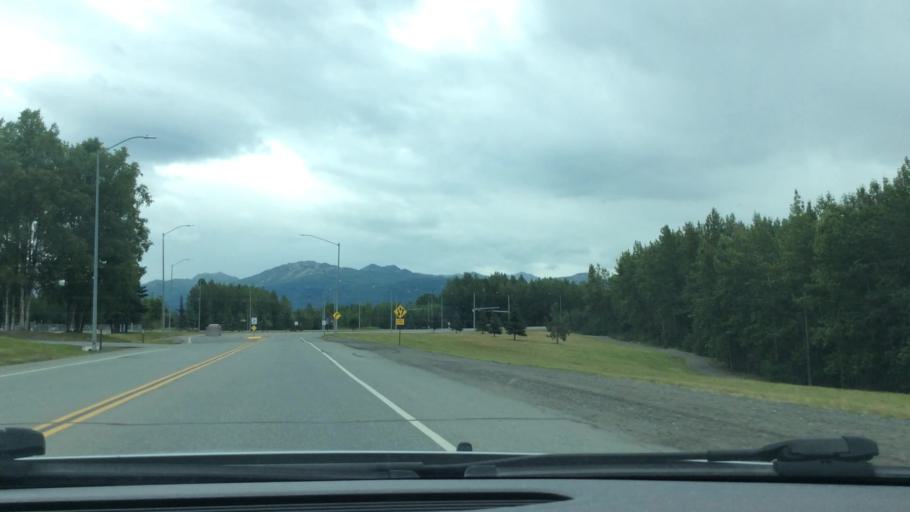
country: US
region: Alaska
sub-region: Anchorage Municipality
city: Anchorage
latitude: 61.2404
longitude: -149.7853
